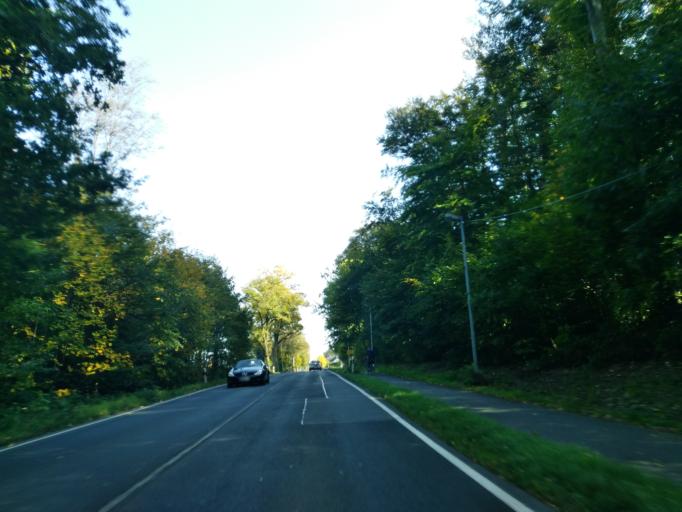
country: DE
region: North Rhine-Westphalia
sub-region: Regierungsbezirk Koln
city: Hennef
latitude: 50.7432
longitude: 7.3491
